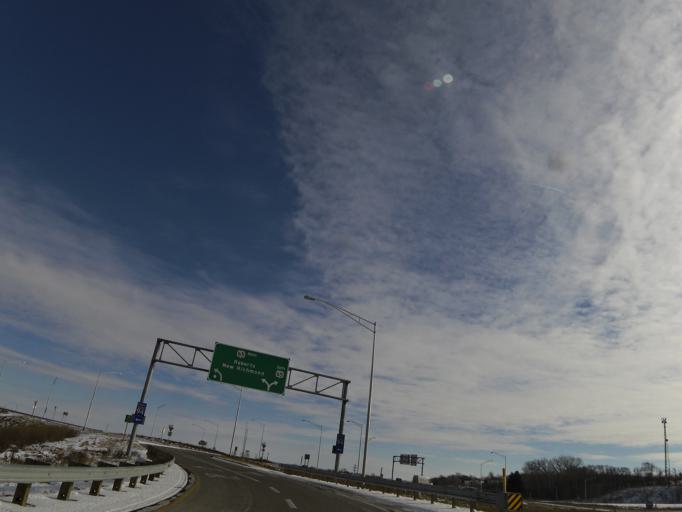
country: US
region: Wisconsin
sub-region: Saint Croix County
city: Roberts
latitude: 44.9587
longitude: -92.5614
